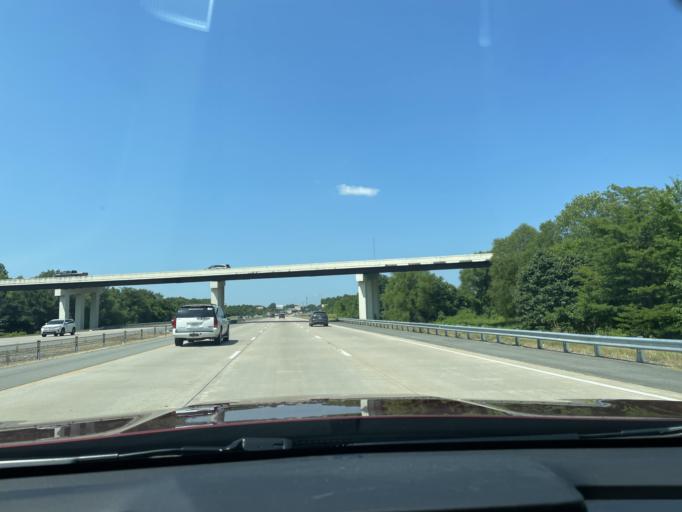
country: US
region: Arkansas
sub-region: Pulaski County
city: McAlmont
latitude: 34.8415
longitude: -92.1577
